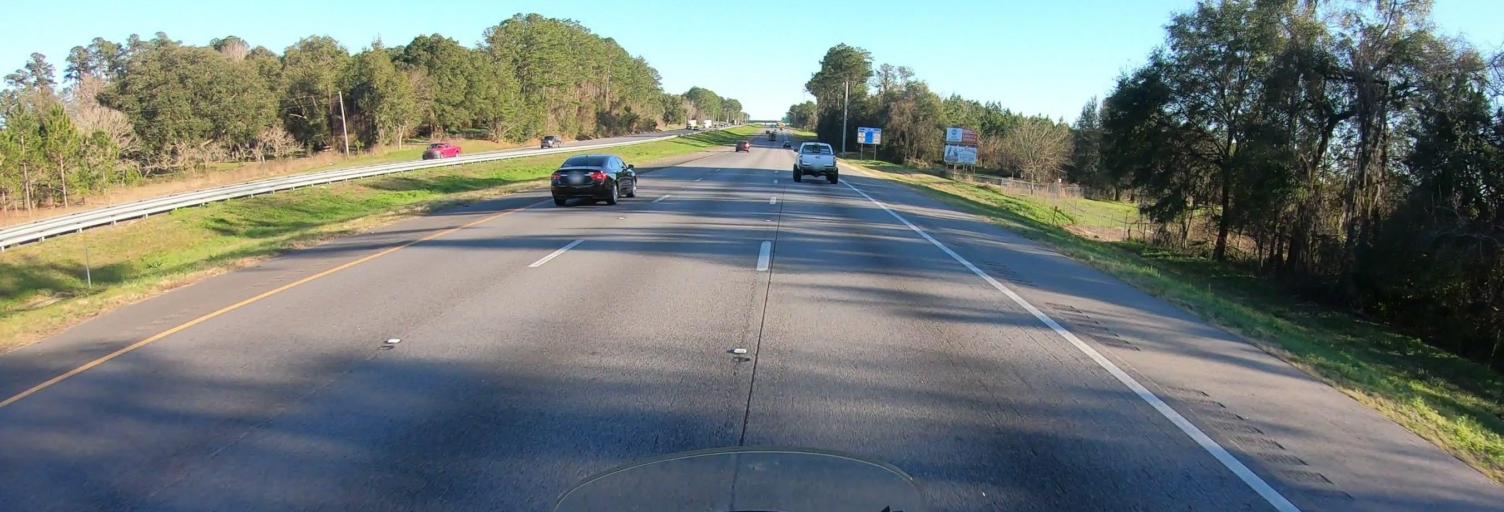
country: US
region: Florida
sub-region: Alachua County
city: Alachua
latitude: 29.6965
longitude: -82.4529
